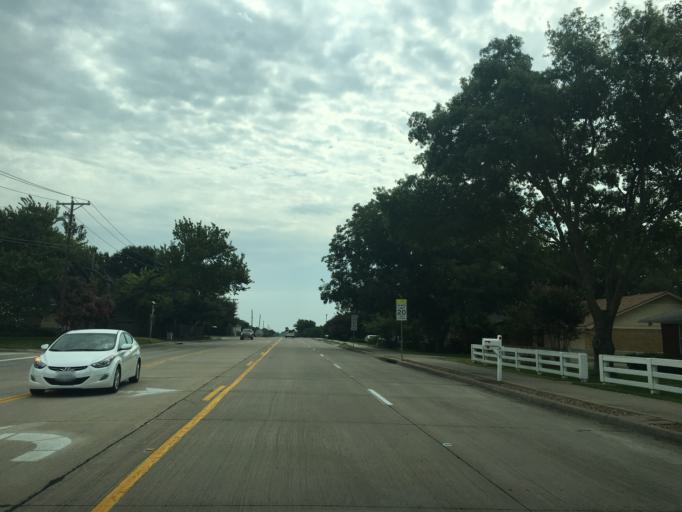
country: US
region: Texas
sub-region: Collin County
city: Wylie
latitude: 33.0060
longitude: -96.5322
